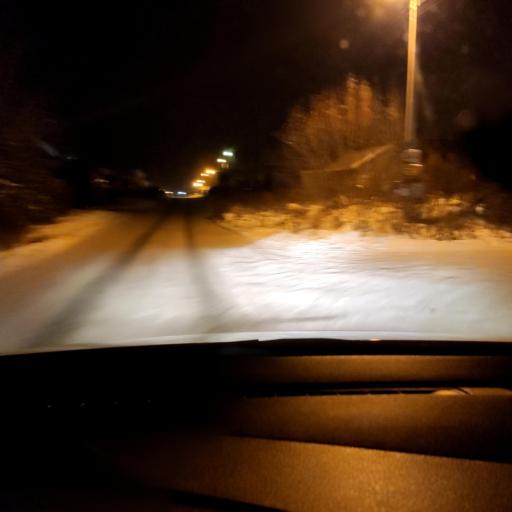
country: RU
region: Tatarstan
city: Stolbishchi
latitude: 55.7508
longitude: 49.2689
